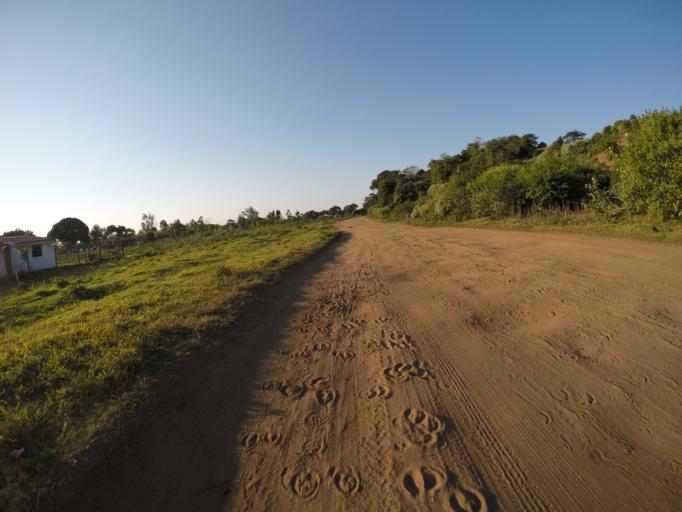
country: ZA
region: KwaZulu-Natal
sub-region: uThungulu District Municipality
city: KwaMbonambi
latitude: -28.7075
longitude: 32.1849
